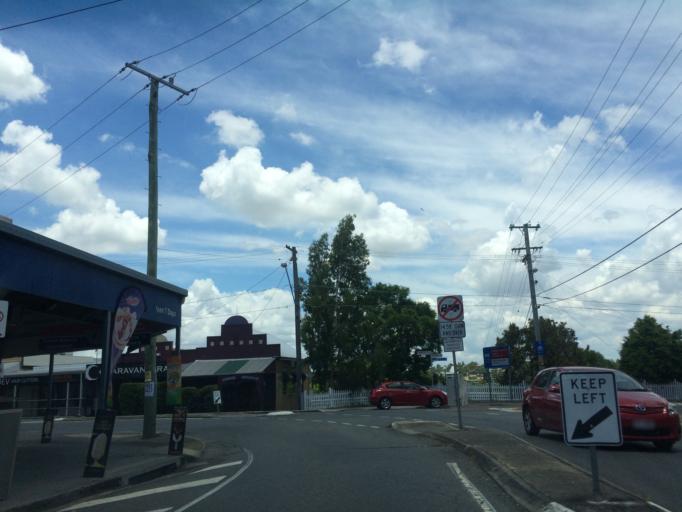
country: AU
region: Queensland
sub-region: Brisbane
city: South Brisbane
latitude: -27.4865
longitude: 153.0062
